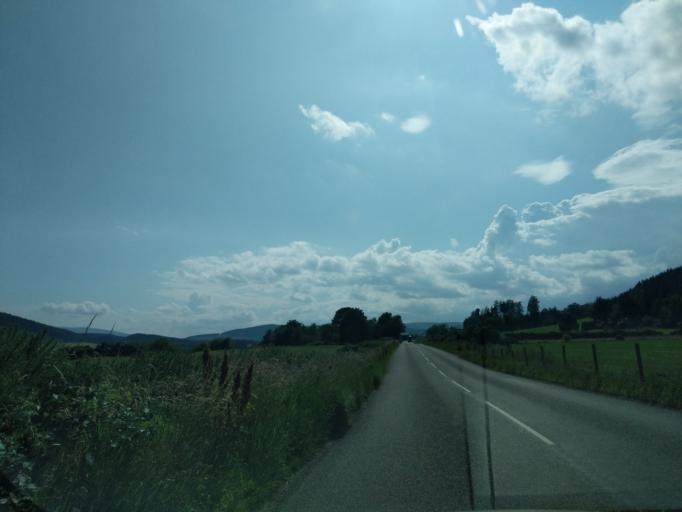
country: GB
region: Scotland
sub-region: Moray
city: Rothes
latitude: 57.5464
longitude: -3.1696
